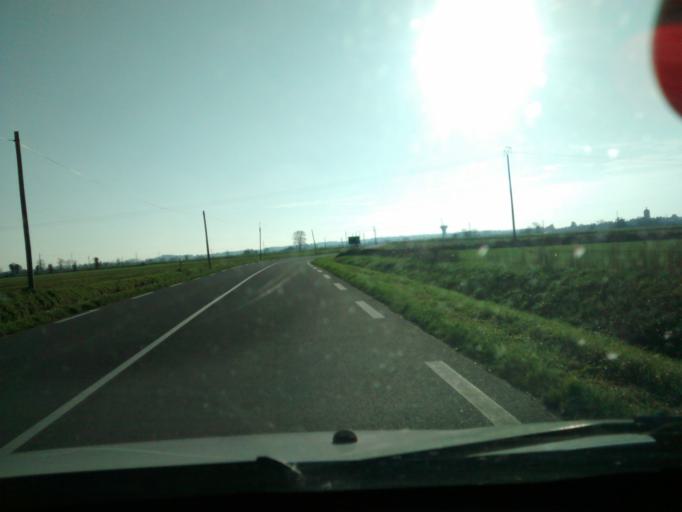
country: FR
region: Brittany
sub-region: Departement d'Ille-et-Vilaine
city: Antrain
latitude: 48.4721
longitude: -1.4753
